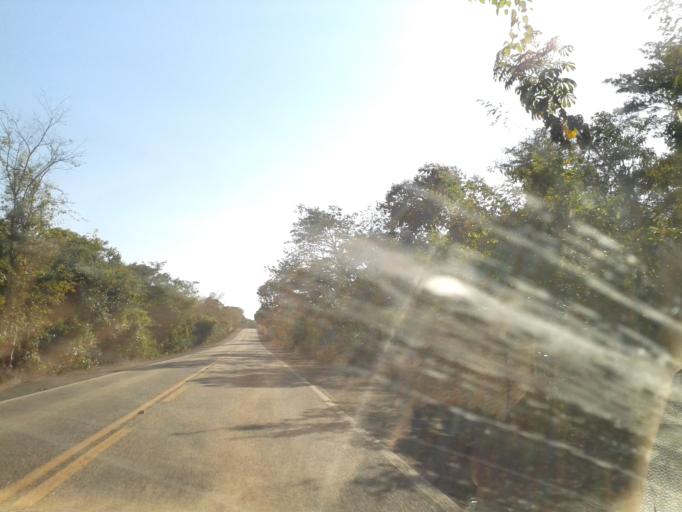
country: BR
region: Goias
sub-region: Mozarlandia
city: Mozarlandia
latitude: -14.9986
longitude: -50.5883
